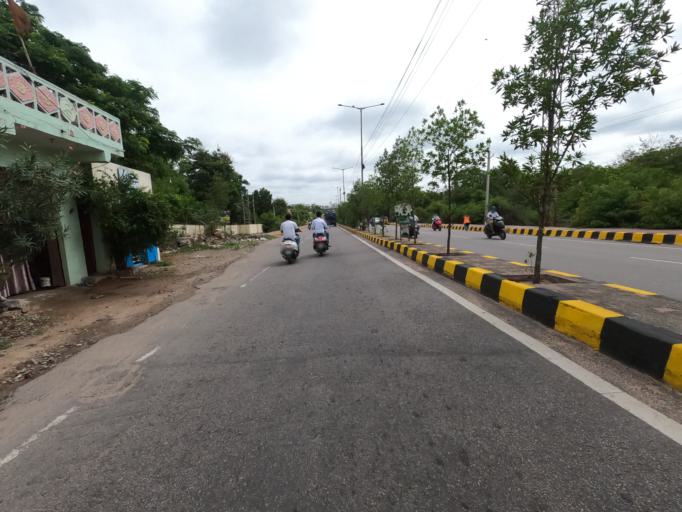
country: IN
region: Telangana
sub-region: Hyderabad
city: Hyderabad
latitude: 17.3382
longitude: 78.4124
